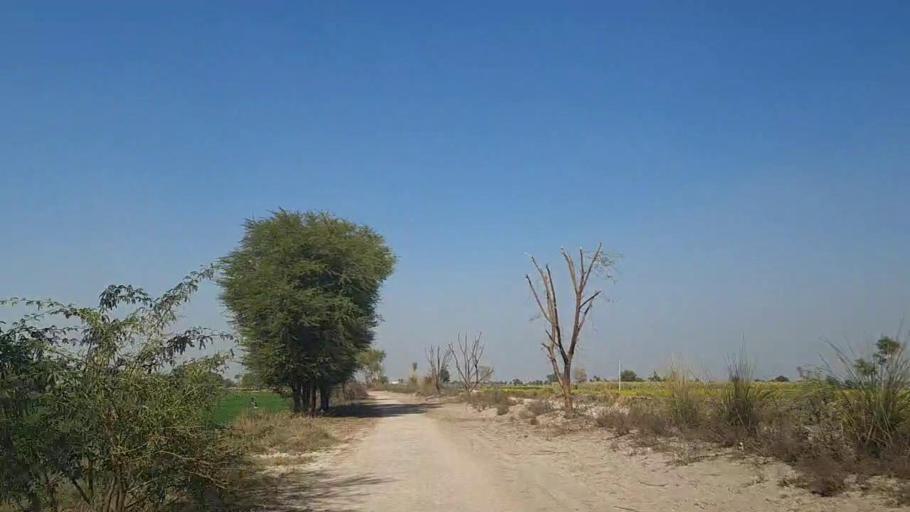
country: PK
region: Sindh
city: Sakrand
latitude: 26.2700
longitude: 68.2210
